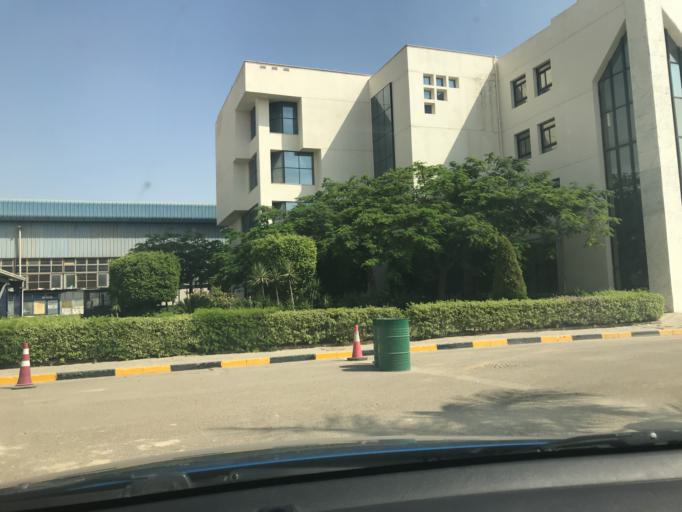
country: EG
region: Eastern Province
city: Bilbays
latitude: 30.2473
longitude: 31.7585
